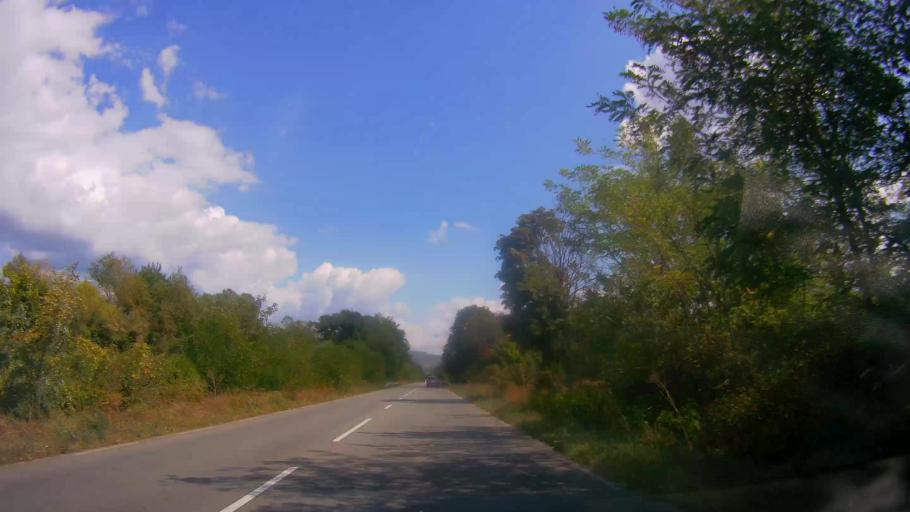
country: BG
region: Sliven
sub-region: Obshtina Tvurditsa
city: Tvurditsa
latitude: 42.6539
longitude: 25.9526
